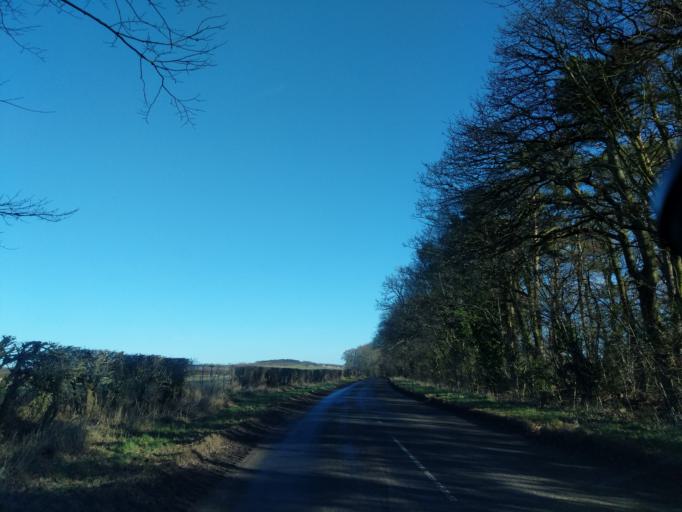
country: GB
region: Scotland
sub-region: East Lothian
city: Haddington
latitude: 55.9606
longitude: -2.7250
